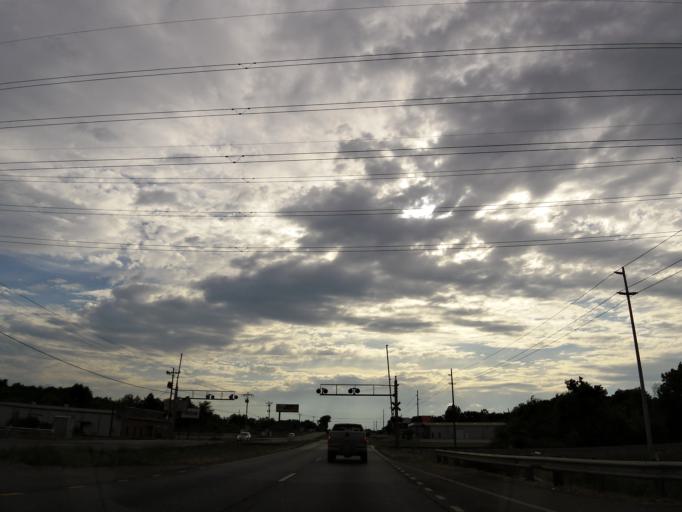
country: US
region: Alabama
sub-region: Morgan County
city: Decatur
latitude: 34.6195
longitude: -87.0323
